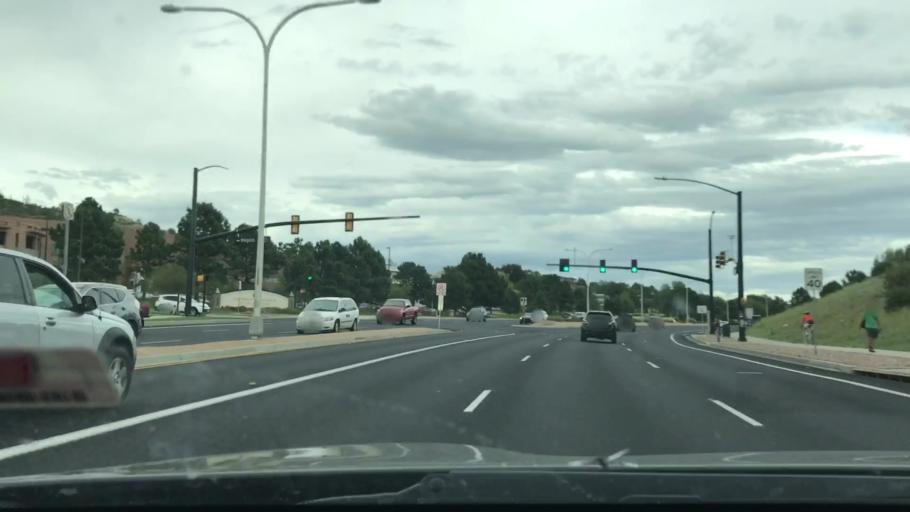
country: US
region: Colorado
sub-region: El Paso County
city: Colorado Springs
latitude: 38.8912
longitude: -104.8027
